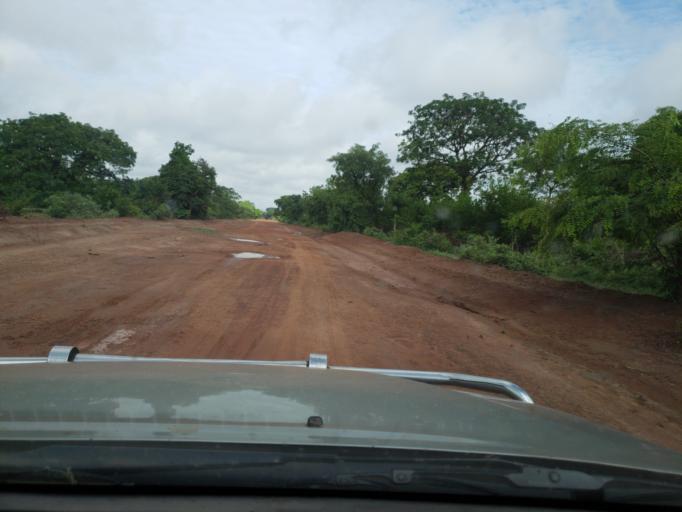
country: ML
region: Sikasso
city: Koutiala
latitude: 12.3925
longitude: -6.0179
